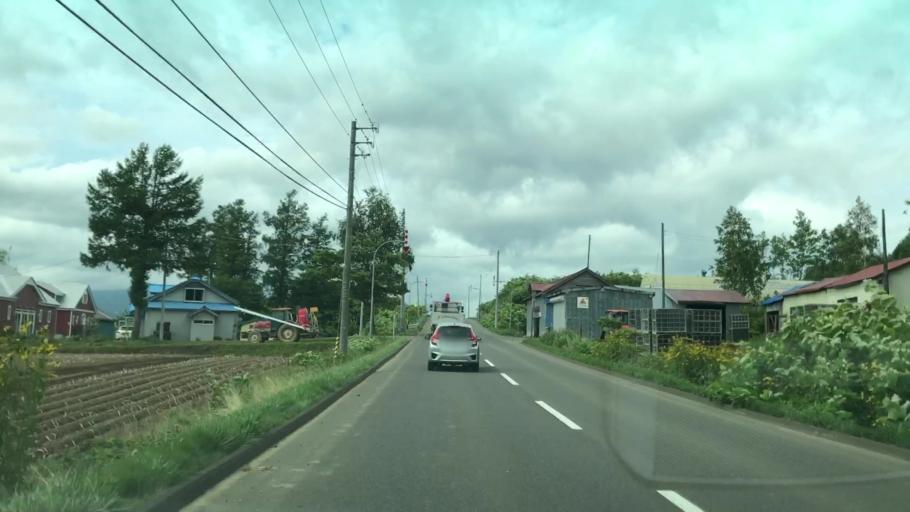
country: JP
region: Hokkaido
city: Niseko Town
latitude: 42.9322
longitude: 140.7928
